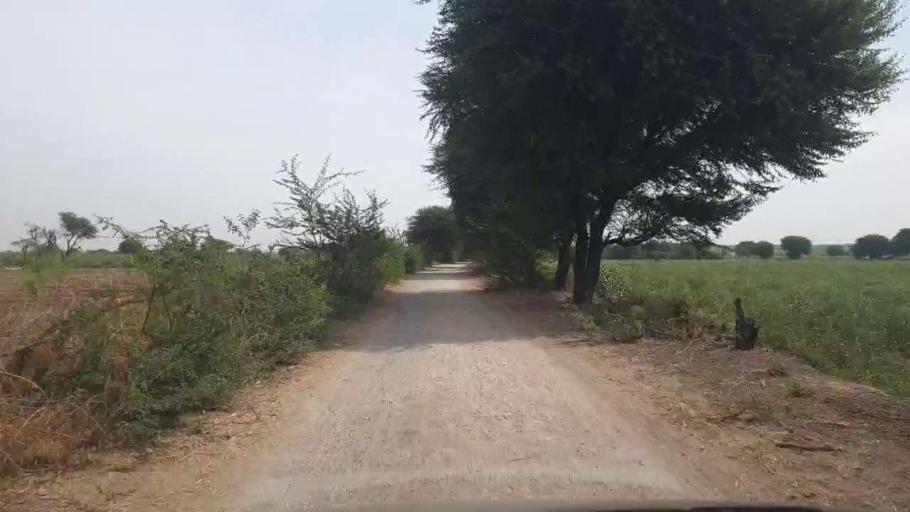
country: PK
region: Sindh
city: Umarkot
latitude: 25.2535
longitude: 69.7121
